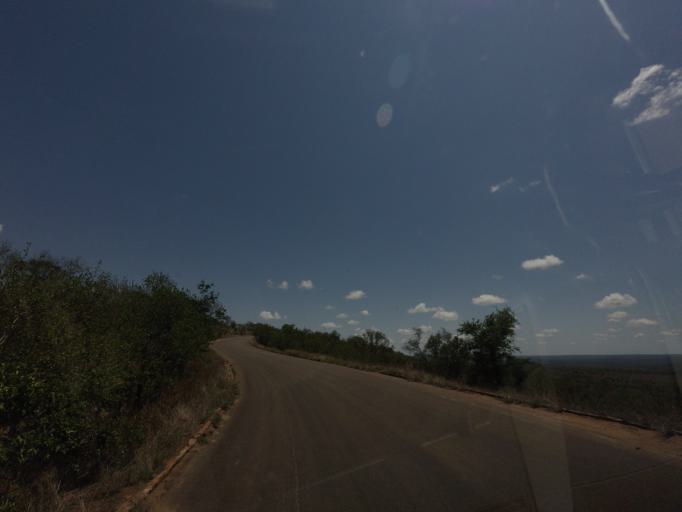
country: ZA
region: Mpumalanga
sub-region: Ehlanzeni District
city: Komatipoort
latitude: -24.8528
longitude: 31.8945
